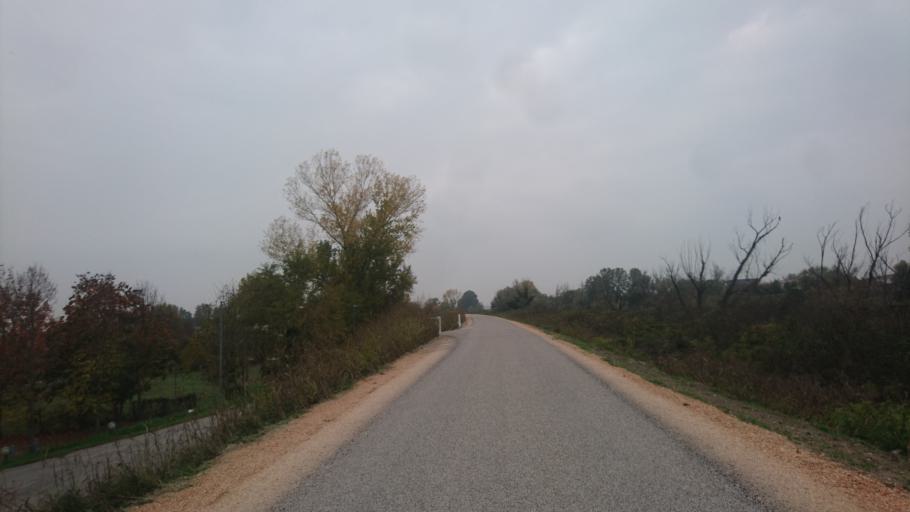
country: IT
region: Veneto
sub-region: Provincia di Padova
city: Oltre Brenta
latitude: 45.4121
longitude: 11.9928
